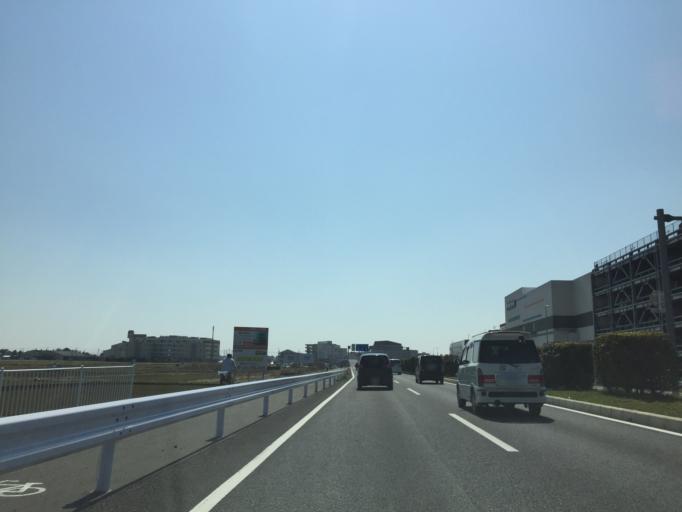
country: JP
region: Saitama
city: Oi
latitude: 35.8628
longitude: 139.5479
